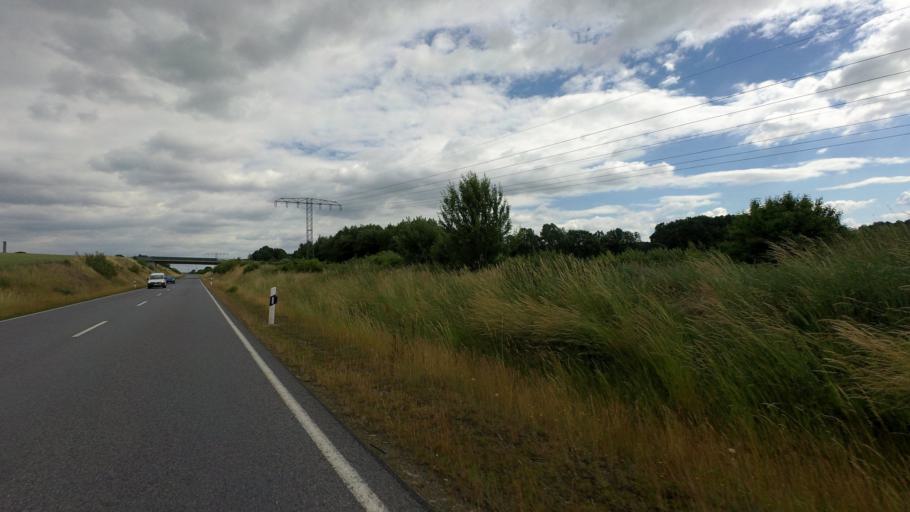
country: DE
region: Saxony
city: Nebelschutz
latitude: 51.2603
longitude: 14.1515
